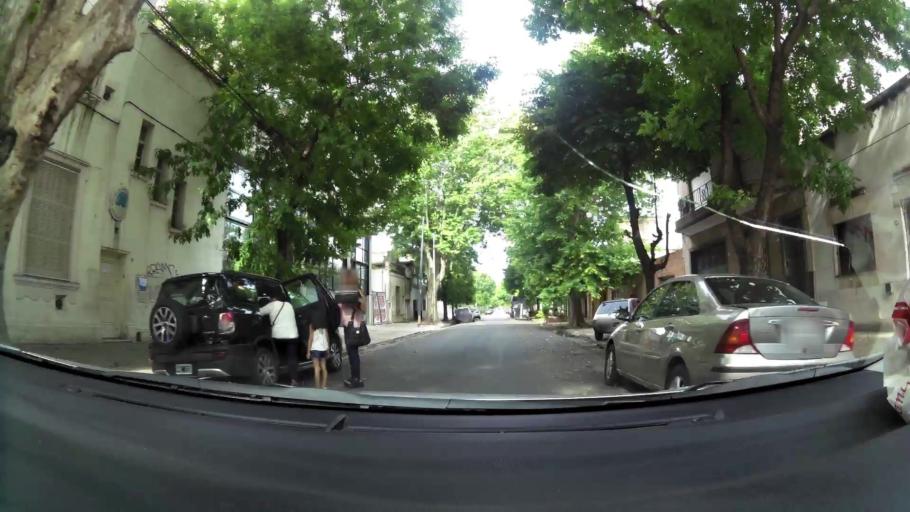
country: AR
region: Buenos Aires F.D.
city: Buenos Aires
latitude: -34.6436
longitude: -58.4209
